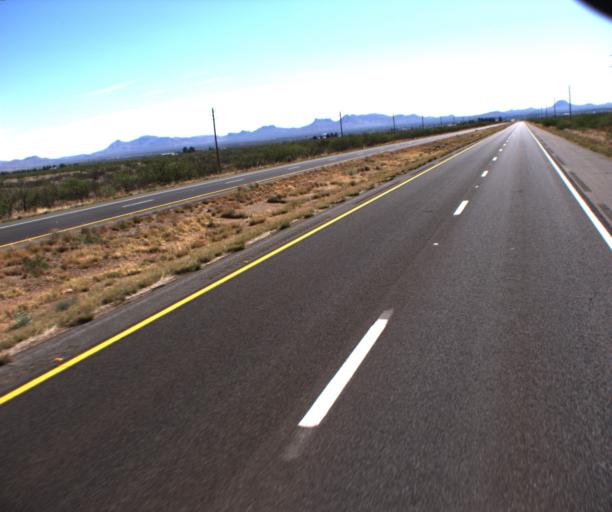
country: US
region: Arizona
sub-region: Cochise County
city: Pirtleville
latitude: 31.3585
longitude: -109.6447
